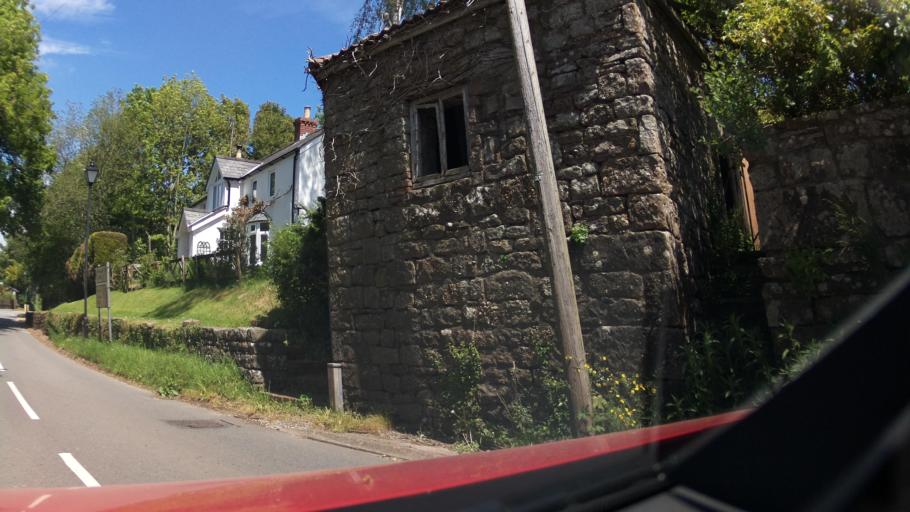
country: GB
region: Wales
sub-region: Monmouthshire
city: Mitchel Troy
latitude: 51.7467
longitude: -2.7256
